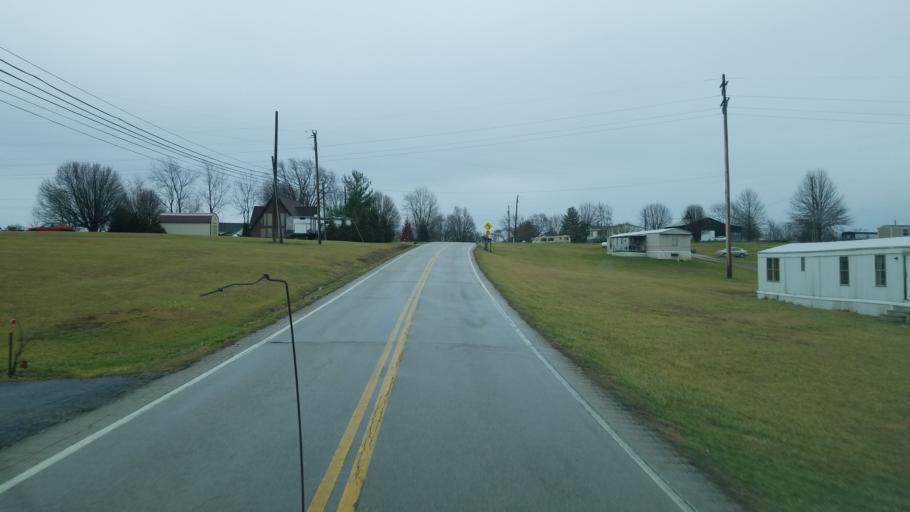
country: US
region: Kentucky
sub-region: Mason County
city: Maysville
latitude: 38.5869
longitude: -83.6610
